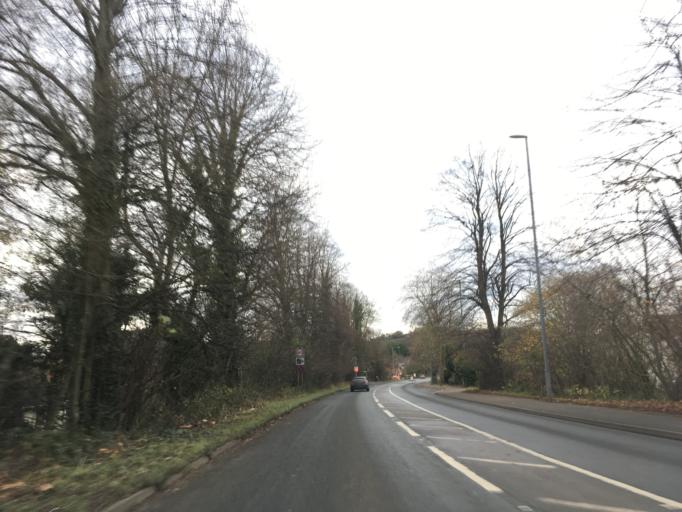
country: GB
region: Wales
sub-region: Newport
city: Langstone
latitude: 51.6052
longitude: -2.9034
